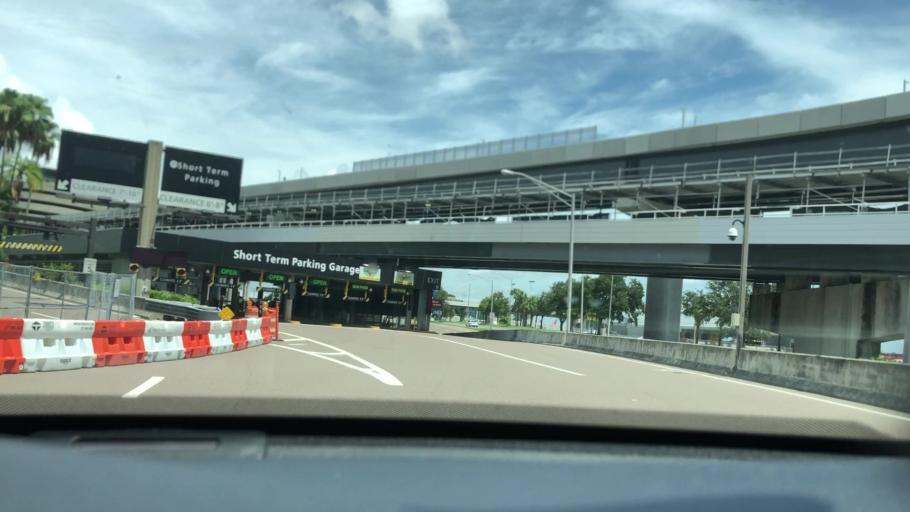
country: US
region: Florida
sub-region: Hillsborough County
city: Egypt Lake-Leto
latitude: 27.9775
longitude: -82.5332
